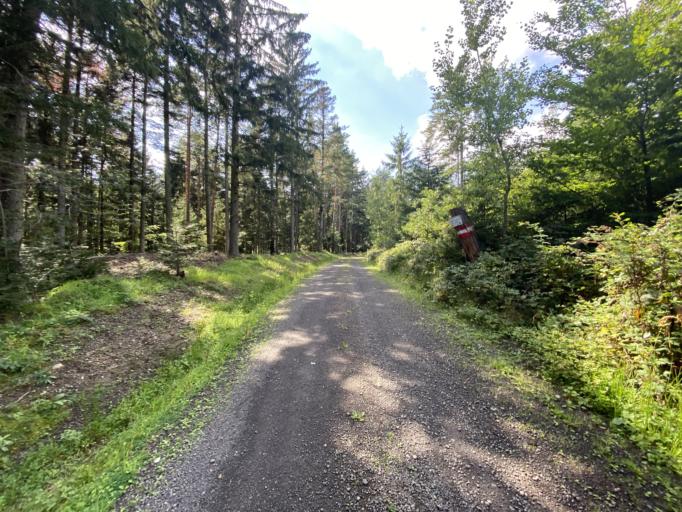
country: AT
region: Burgenland
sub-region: Politischer Bezirk Oberpullendorf
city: Kobersdorf
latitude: 47.5785
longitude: 16.3704
